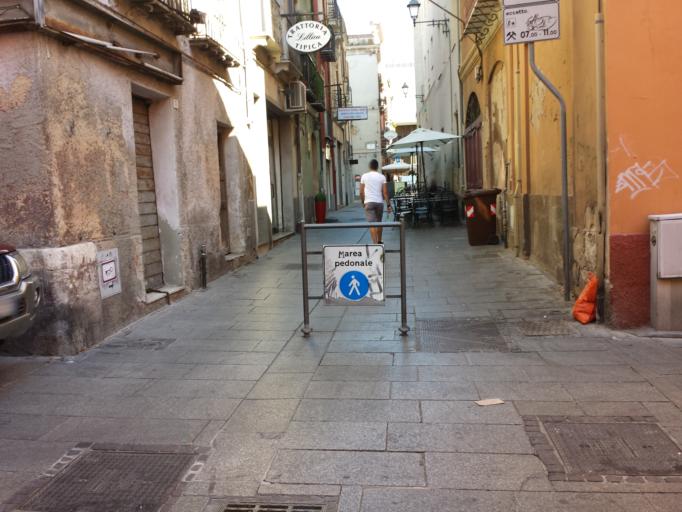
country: IT
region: Sardinia
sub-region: Provincia di Cagliari
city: Cagliari
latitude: 39.2142
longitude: 9.1133
